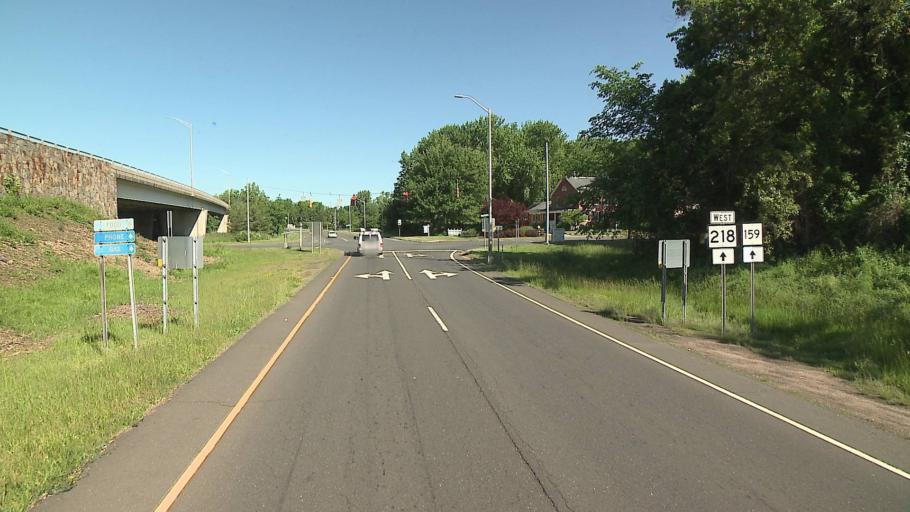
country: US
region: Connecticut
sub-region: Hartford County
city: South Windsor
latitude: 41.8173
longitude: -72.6548
